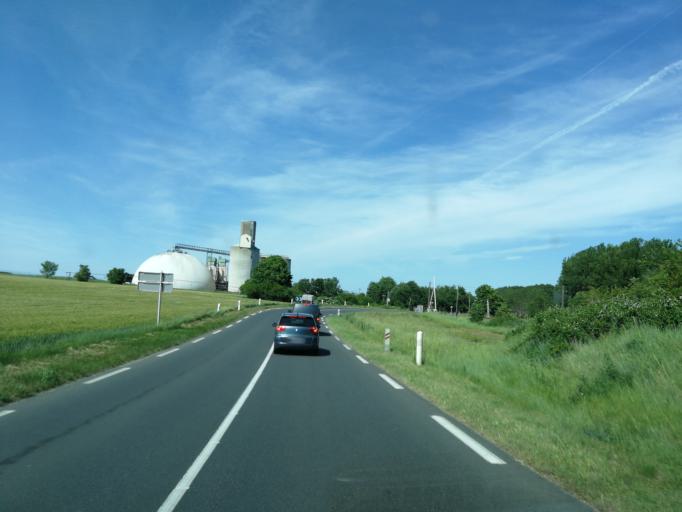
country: FR
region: Poitou-Charentes
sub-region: Departement de la Vienne
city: Loudun
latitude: 47.0643
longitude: 0.1610
